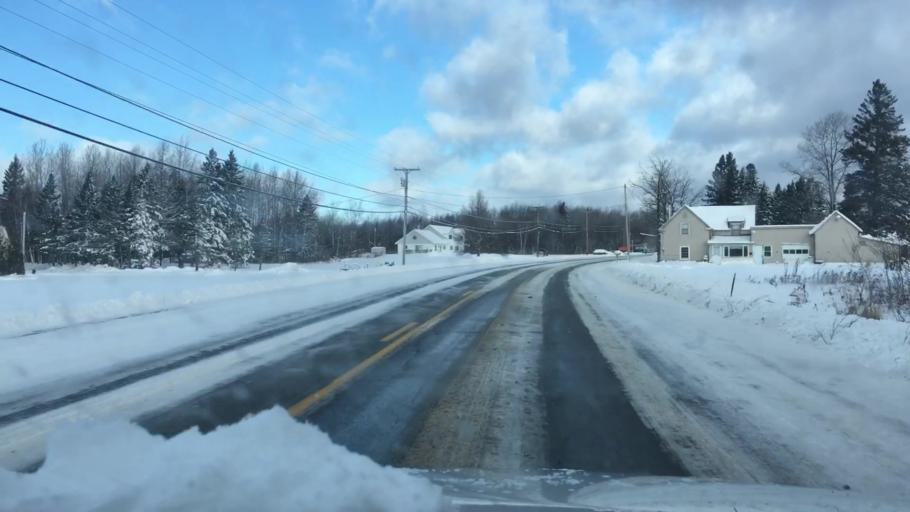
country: US
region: Maine
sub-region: Aroostook County
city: Caribou
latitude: 46.9291
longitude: -68.0226
